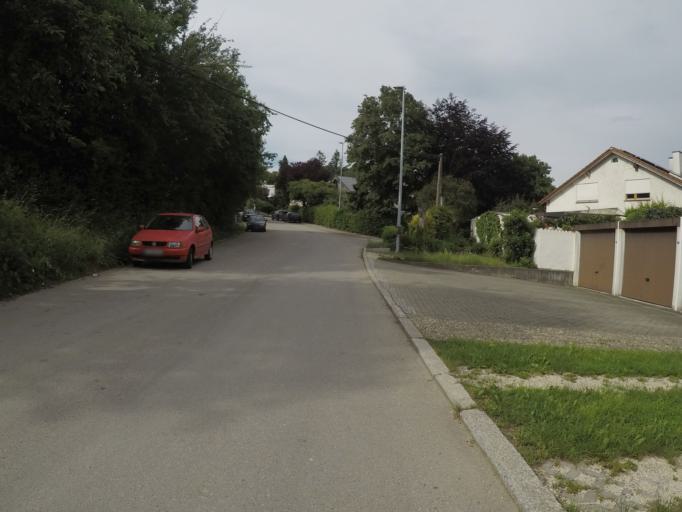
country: DE
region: Baden-Wuerttemberg
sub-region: Tuebingen Region
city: Pfullingen
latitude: 48.4560
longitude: 9.2099
